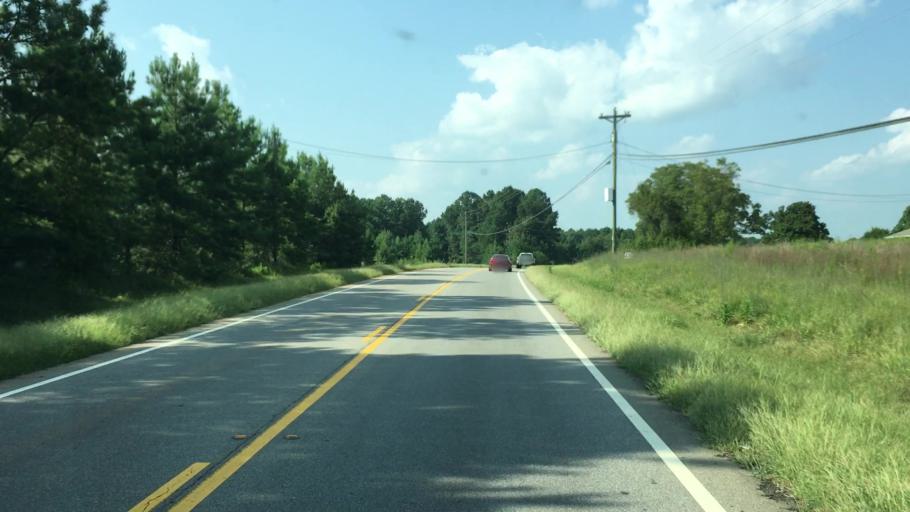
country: US
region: Georgia
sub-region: Walton County
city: Social Circle
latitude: 33.7035
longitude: -83.7025
